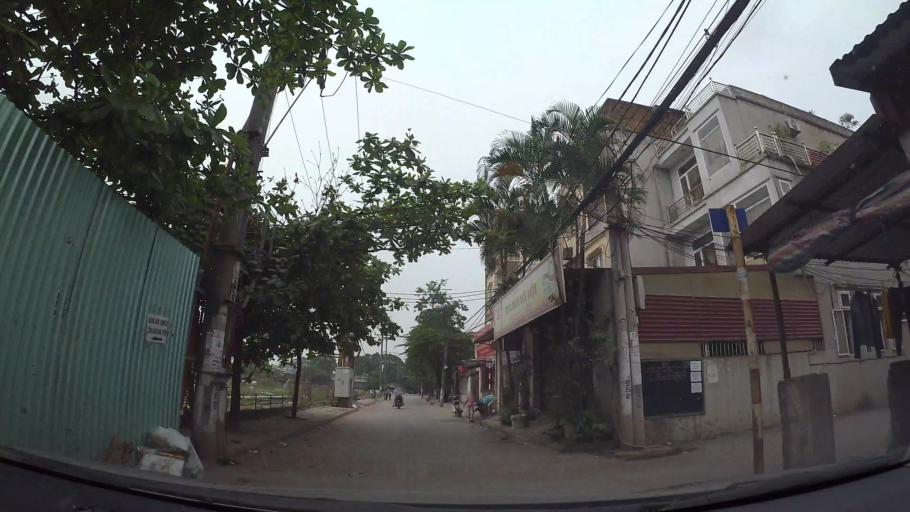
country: VN
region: Ha Noi
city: Hoan Kiem
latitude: 21.0646
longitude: 105.8847
